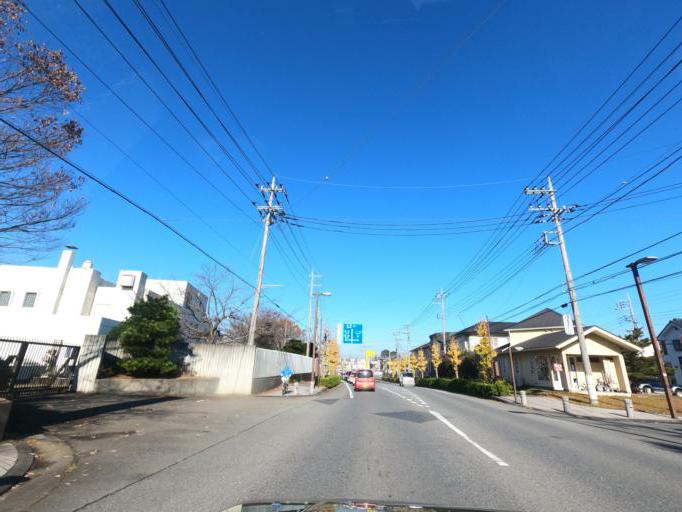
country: JP
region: Ibaraki
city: Mitsukaido
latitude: 35.9810
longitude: 139.9769
